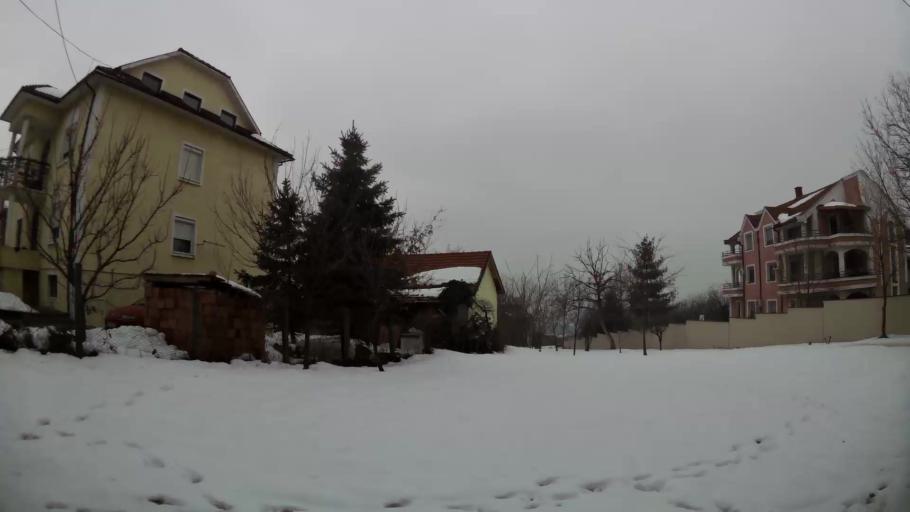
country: RS
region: Central Serbia
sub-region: Belgrade
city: Zvezdara
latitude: 44.7459
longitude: 20.5099
